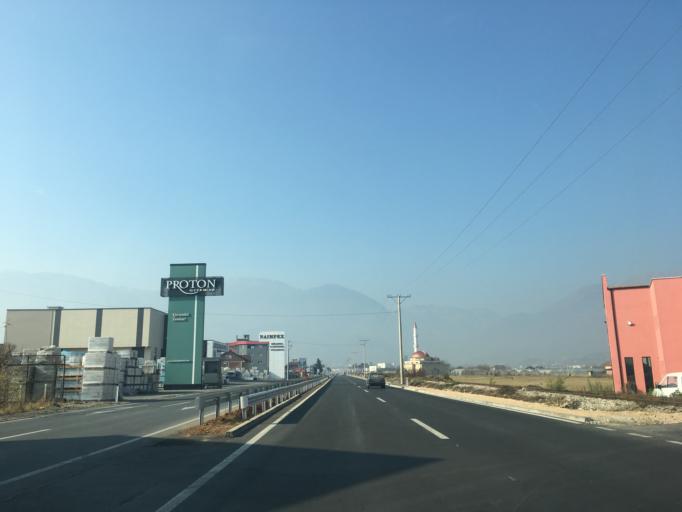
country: XK
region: Pec
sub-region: Komuna e Pejes
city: Peje
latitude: 42.6582
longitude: 20.3407
